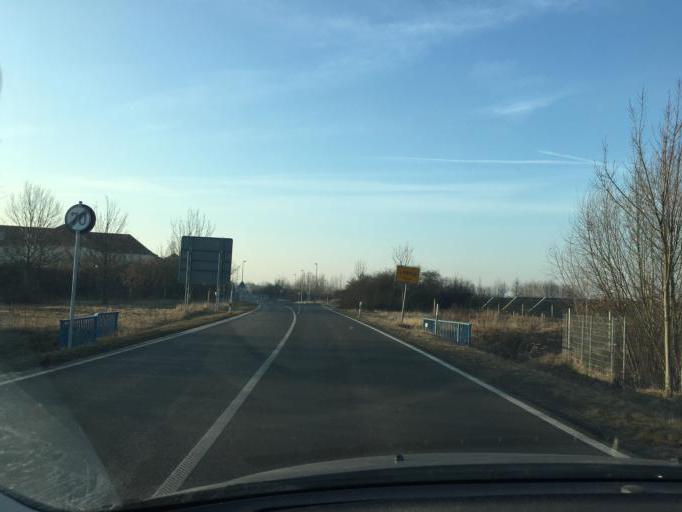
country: DE
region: Saxony
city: Borsdorf
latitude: 51.3485
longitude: 12.5196
